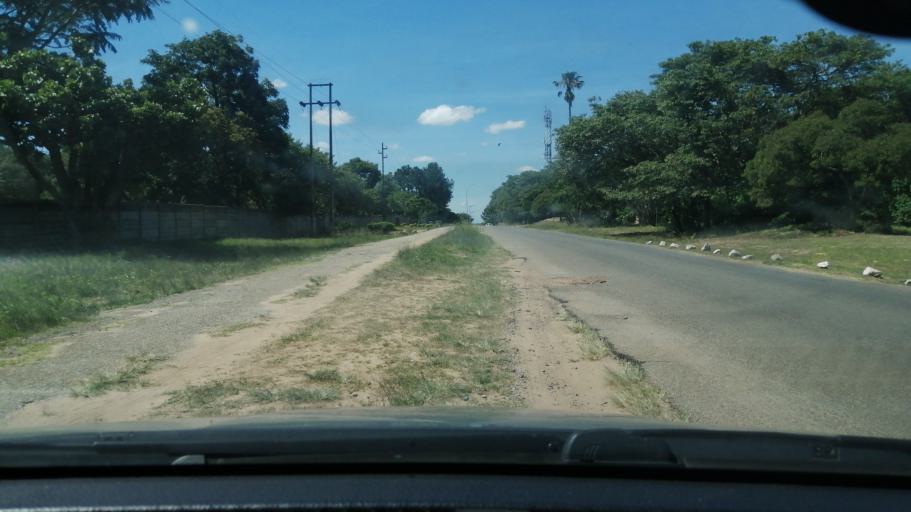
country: ZW
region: Harare
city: Epworth
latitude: -17.8248
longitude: 31.1258
